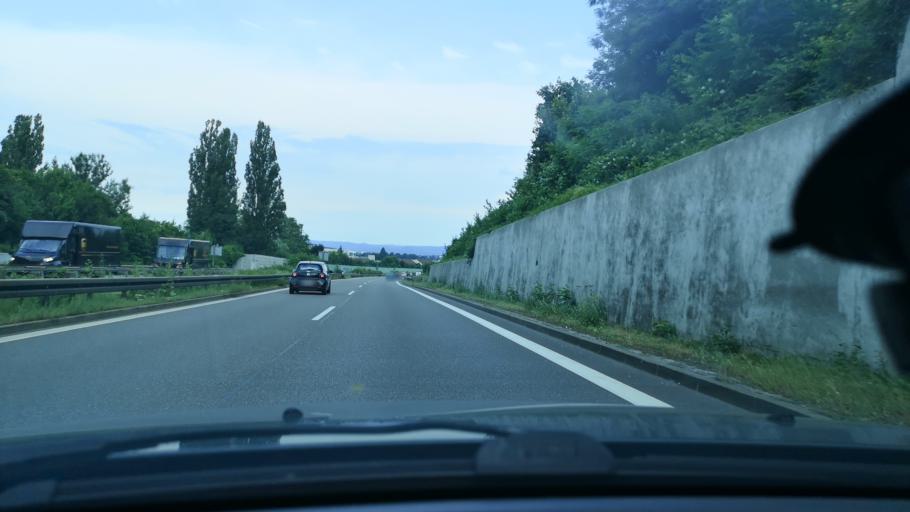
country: DE
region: Baden-Wuerttemberg
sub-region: Regierungsbezirk Stuttgart
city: Goeppingen
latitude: 48.6975
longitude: 9.6494
